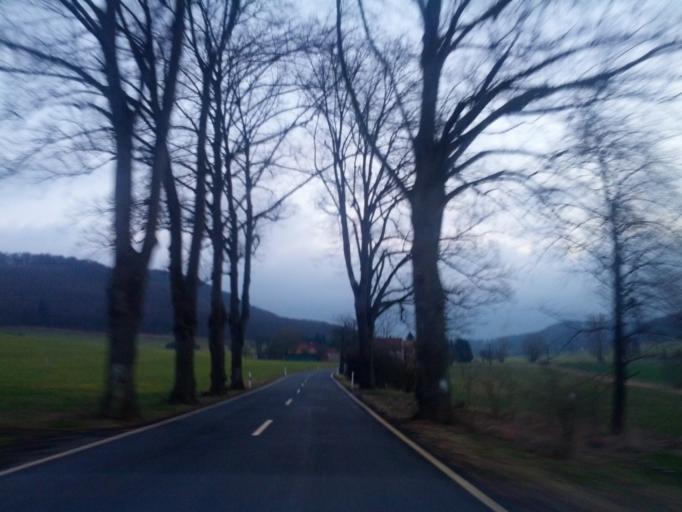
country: DE
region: Thuringia
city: Ifta
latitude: 51.0816
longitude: 10.2155
